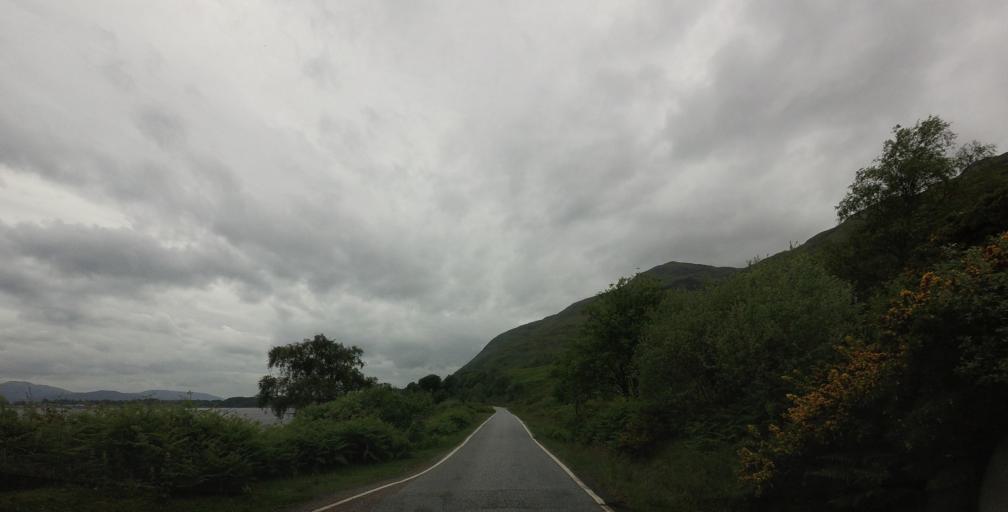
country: GB
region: Scotland
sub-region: Highland
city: Fort William
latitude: 56.7452
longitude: -5.2419
